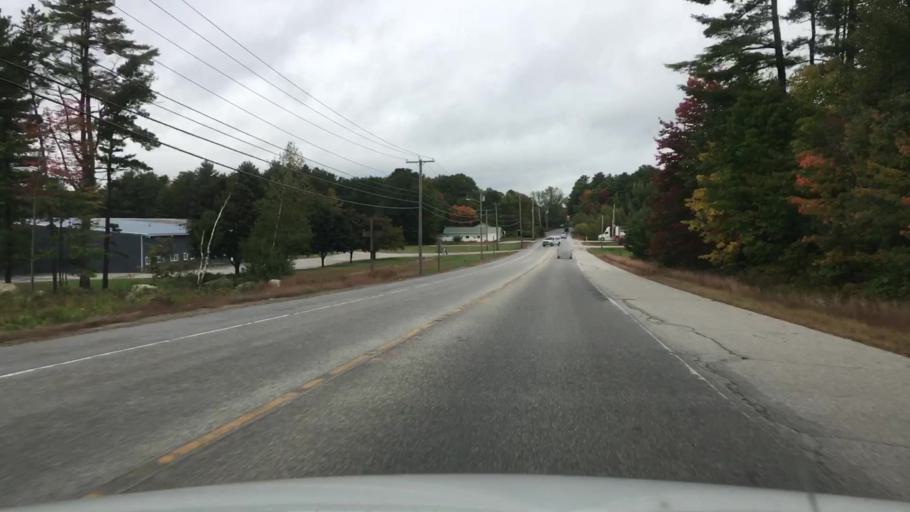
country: US
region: Maine
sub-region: Oxford County
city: Oxford
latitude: 44.1396
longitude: -70.4719
